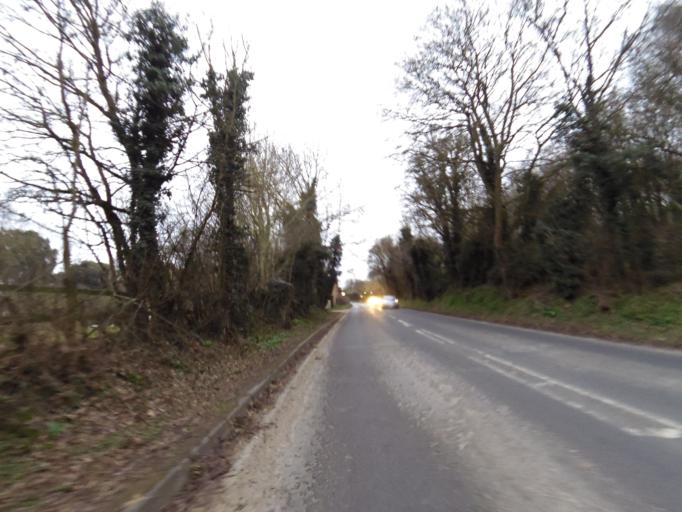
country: GB
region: England
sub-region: Suffolk
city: Ipswich
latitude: 52.0880
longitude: 1.1522
